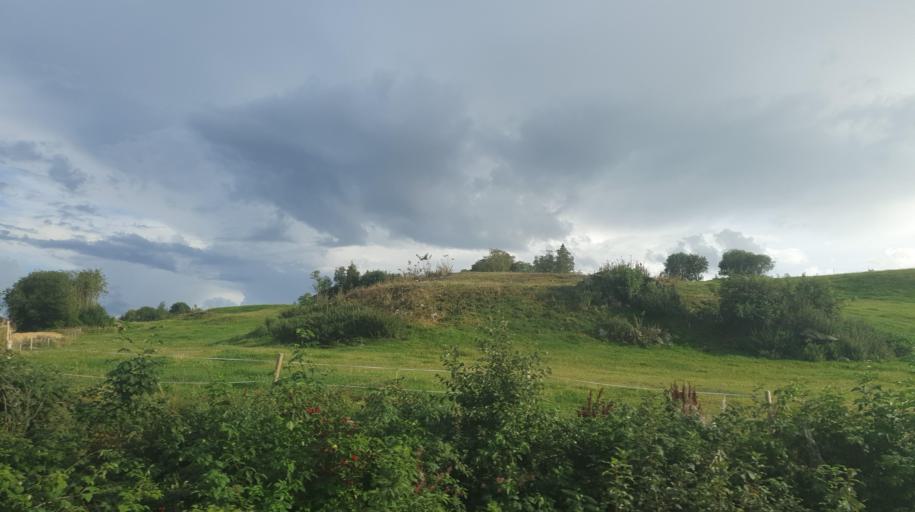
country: NO
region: Nord-Trondelag
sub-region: Levanger
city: Skogn
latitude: 63.7145
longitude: 11.2065
